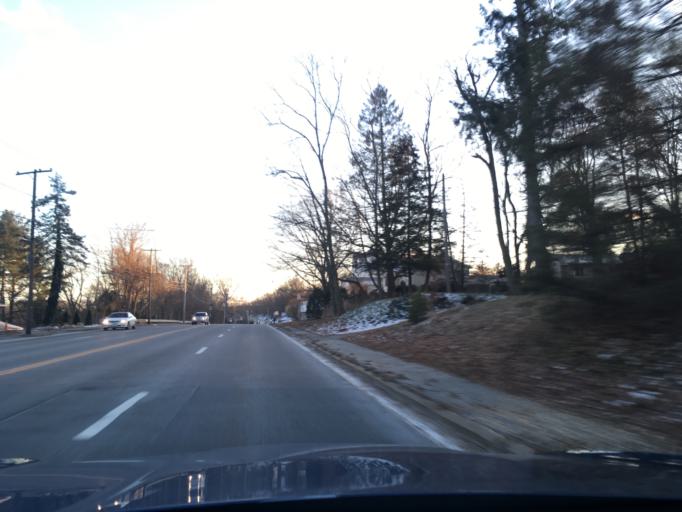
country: US
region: Rhode Island
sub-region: Kent County
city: East Greenwich
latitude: 41.7072
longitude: -71.4634
